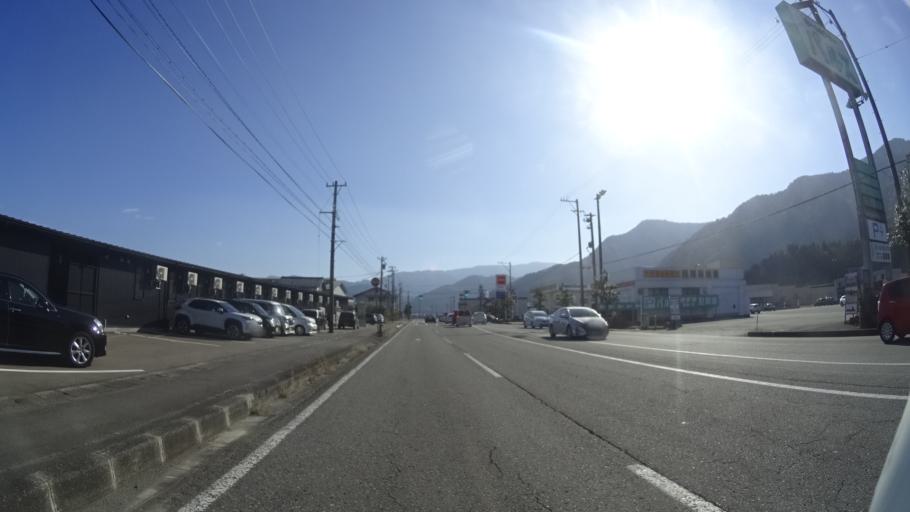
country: JP
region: Fukui
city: Ono
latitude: 35.9766
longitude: 136.4800
